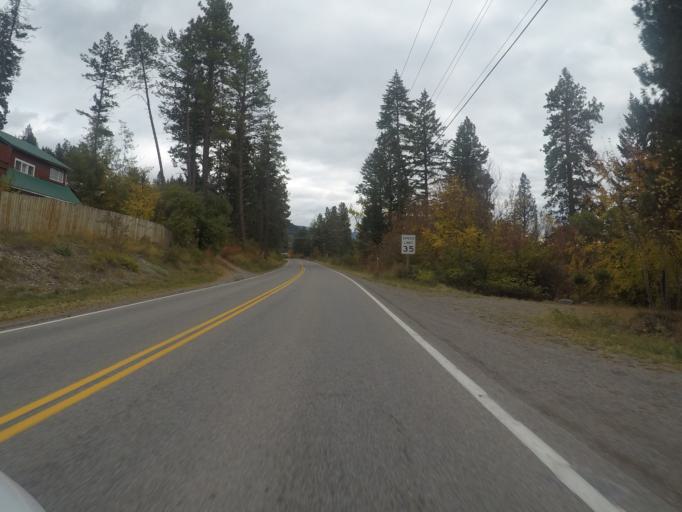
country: US
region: Montana
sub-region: Flathead County
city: Bigfork
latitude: 48.0015
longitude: -114.0505
